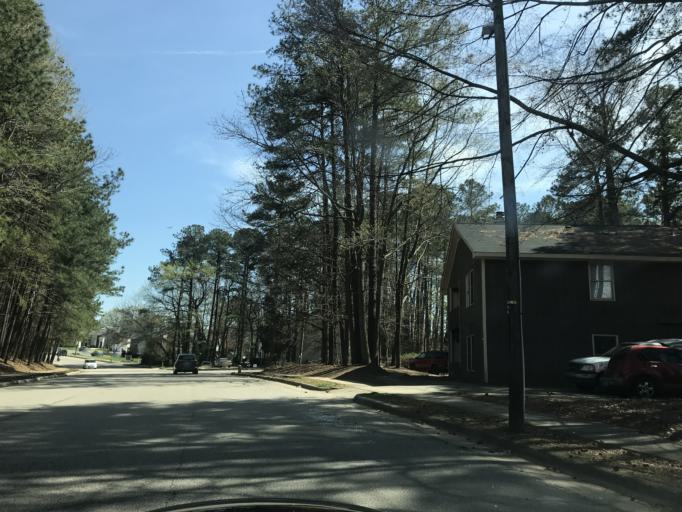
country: US
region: North Carolina
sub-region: Wake County
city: Raleigh
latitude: 35.8399
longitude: -78.5942
